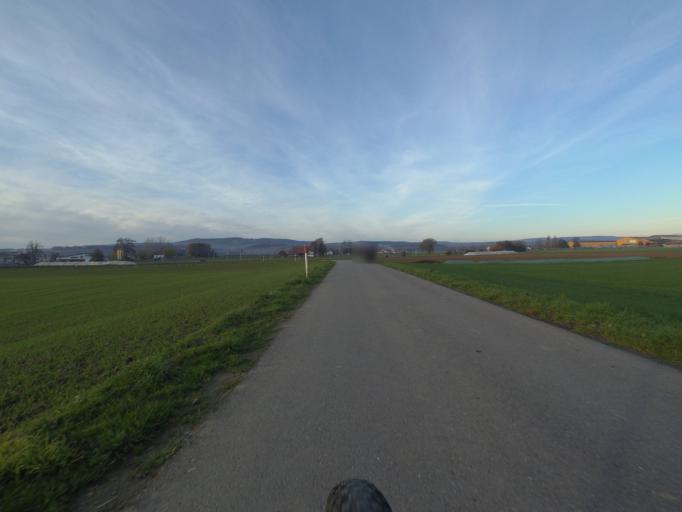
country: CH
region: Thurgau
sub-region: Frauenfeld District
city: Frauenfeld
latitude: 47.5685
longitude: 8.9243
